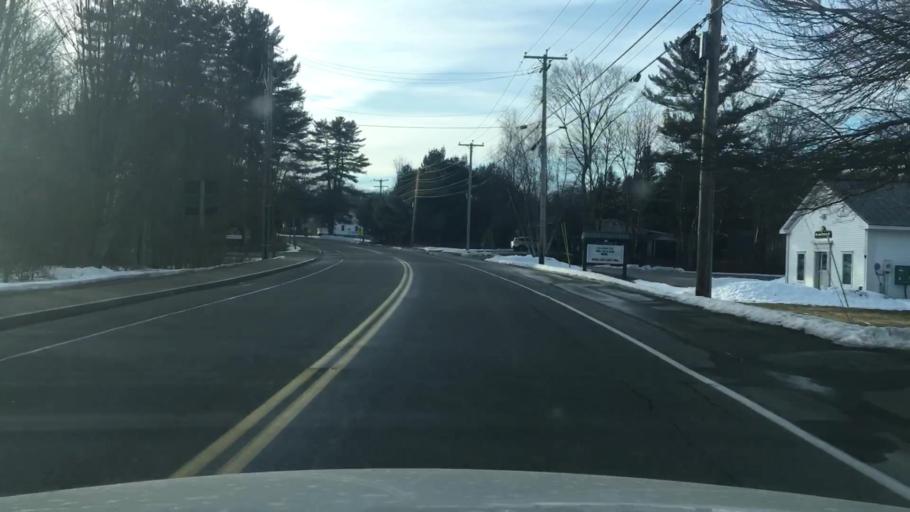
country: US
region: Maine
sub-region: York County
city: Wells Beach Station
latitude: 43.3229
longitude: -70.5863
